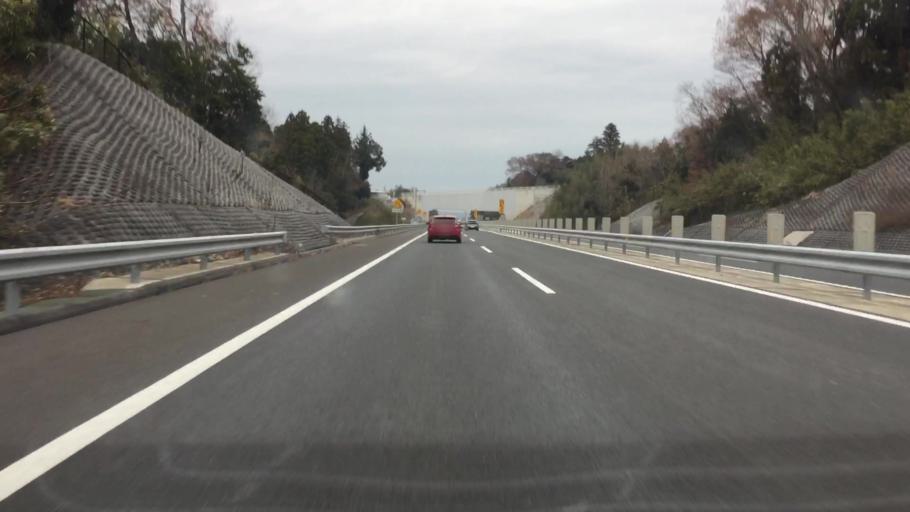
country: JP
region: Ibaraki
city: Edosaki
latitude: 35.8689
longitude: 140.3901
